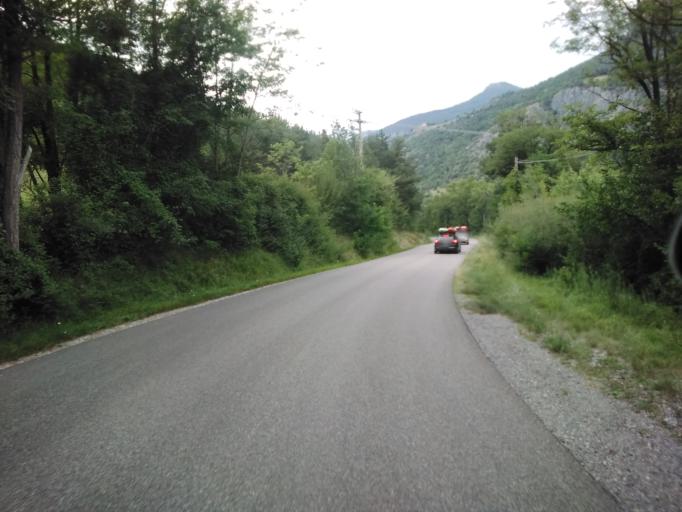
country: FR
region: Provence-Alpes-Cote d'Azur
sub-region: Departement des Alpes-de-Haute-Provence
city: Seyne-les-Alpes
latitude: 44.4503
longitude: 6.3919
